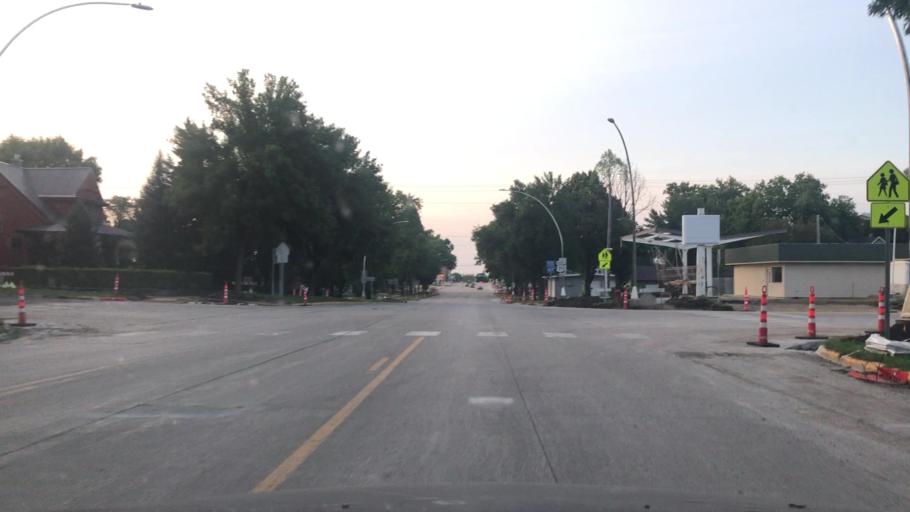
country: US
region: Minnesota
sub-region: Redwood County
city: Redwood Falls
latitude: 44.5348
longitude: -95.1195
